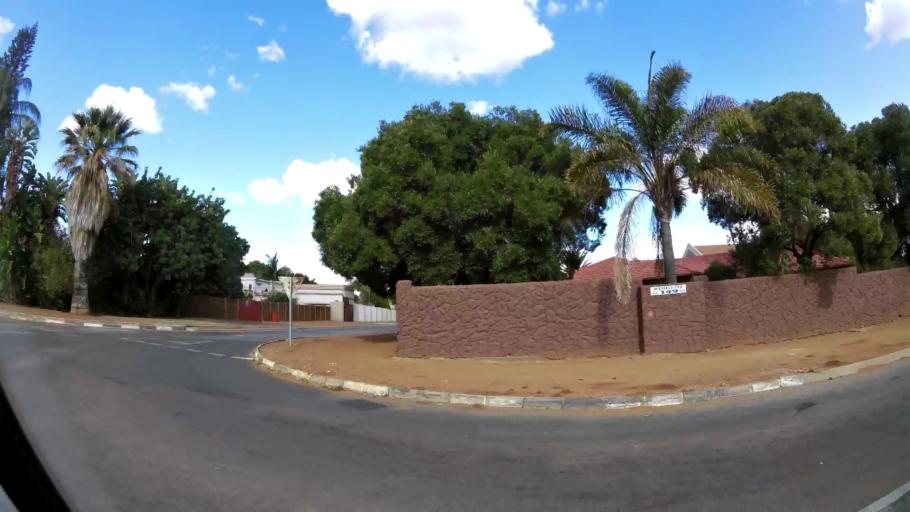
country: ZA
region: Limpopo
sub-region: Capricorn District Municipality
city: Polokwane
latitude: -23.8931
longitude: 29.4793
